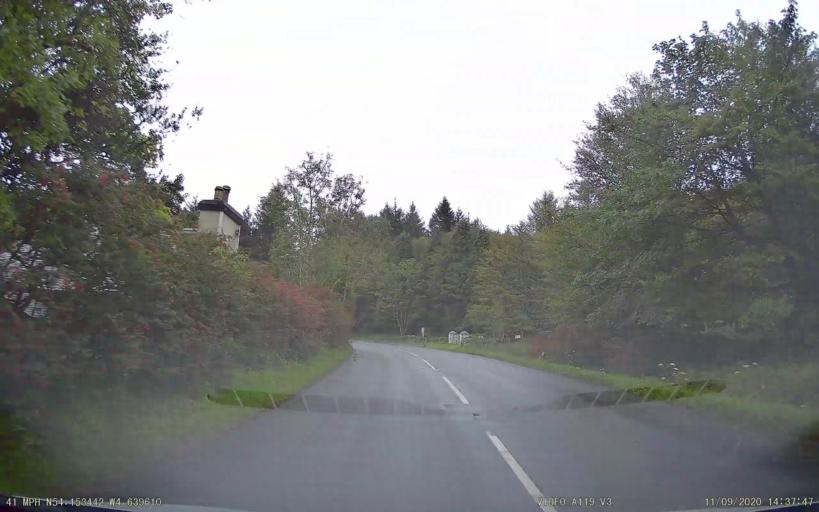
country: IM
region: Castletown
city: Castletown
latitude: 54.1534
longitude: -4.6395
